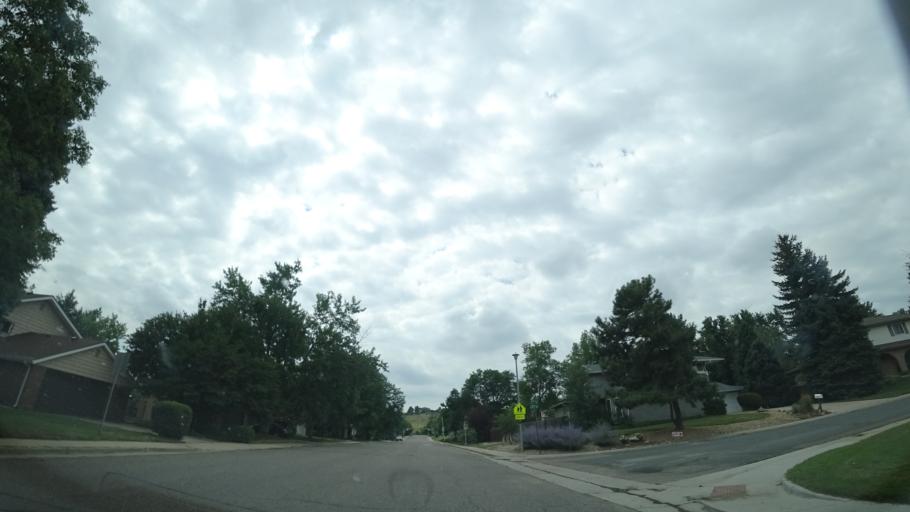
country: US
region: Colorado
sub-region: Jefferson County
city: West Pleasant View
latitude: 39.7215
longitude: -105.1600
